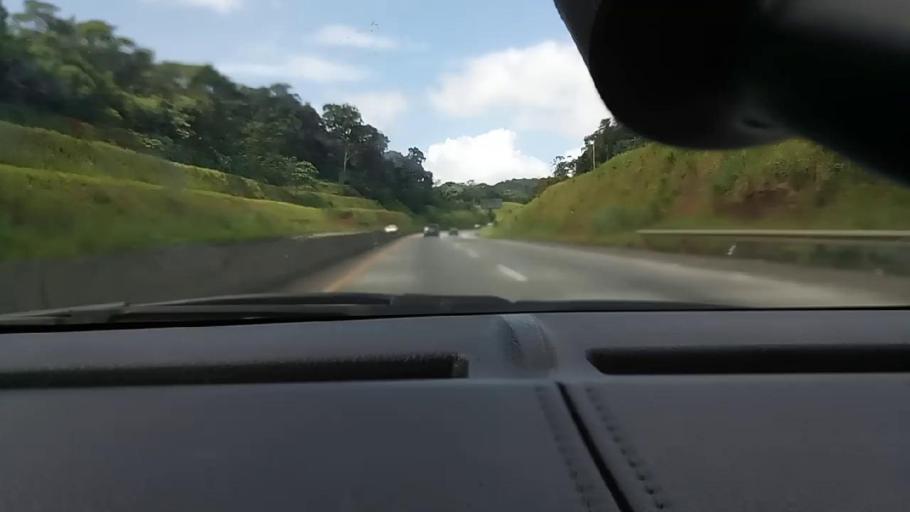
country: PA
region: Colon
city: Gatun
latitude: 9.2825
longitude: -79.7723
